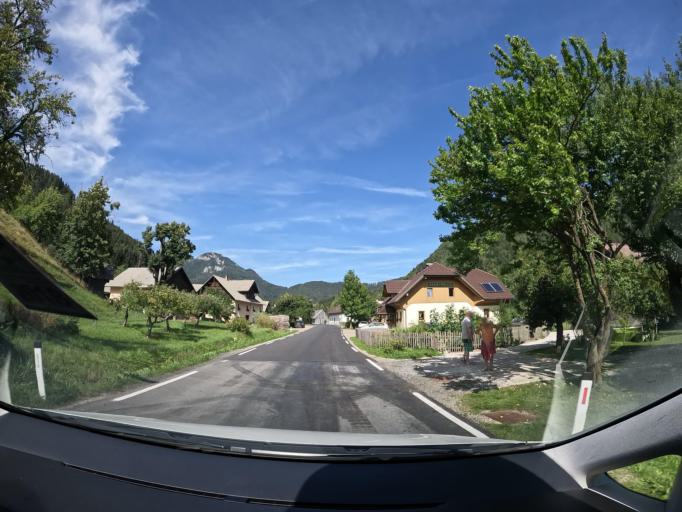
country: AT
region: Carinthia
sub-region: Politischer Bezirk Feldkirchen
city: Feldkirchen in Karnten
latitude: 46.6911
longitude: 14.1233
